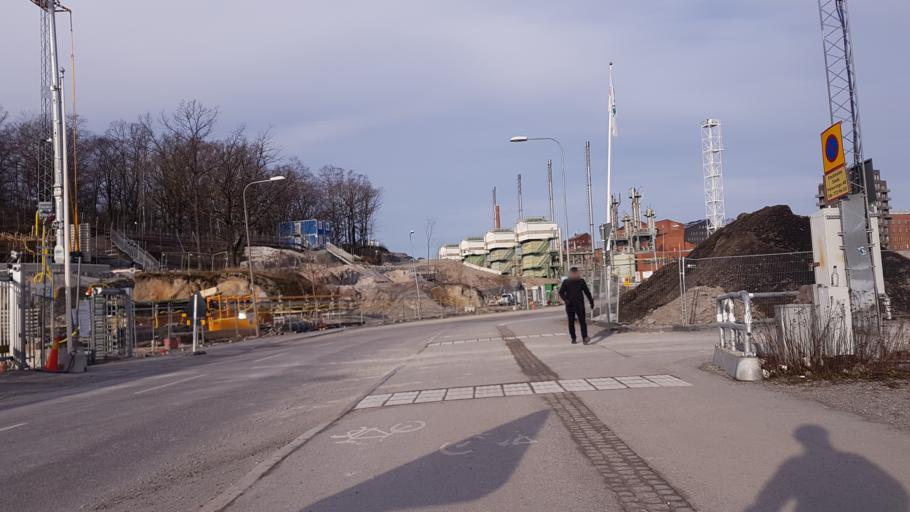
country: SE
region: Stockholm
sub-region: Stockholms Kommun
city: OEstermalm
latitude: 59.3585
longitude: 18.1009
